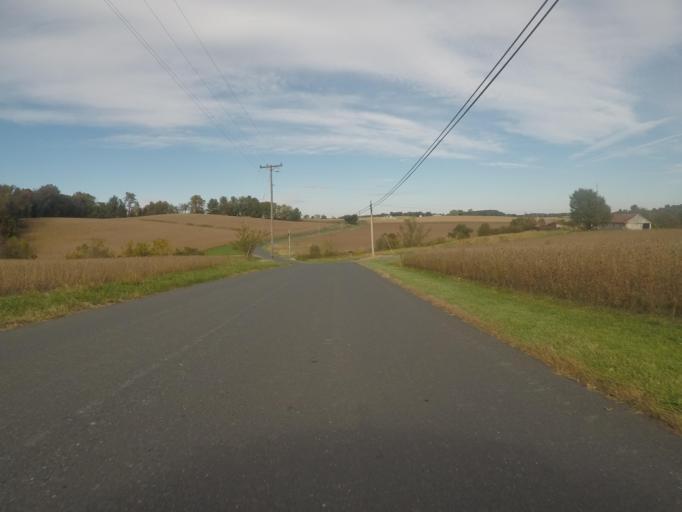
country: US
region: Maryland
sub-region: Carroll County
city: Hampstead
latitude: 39.5445
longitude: -76.8298
